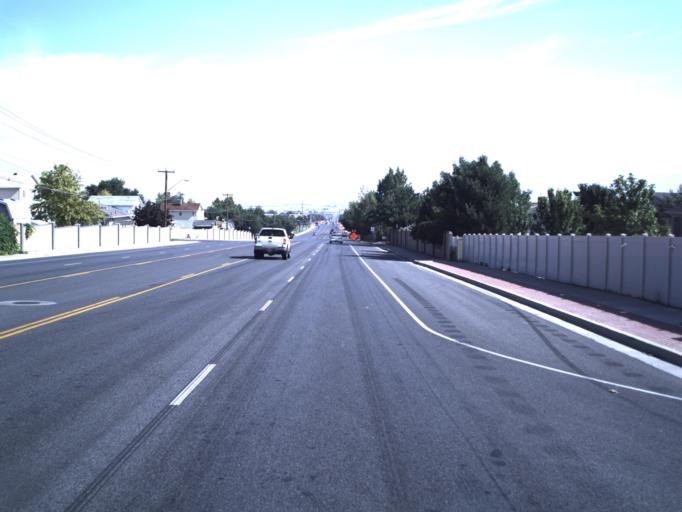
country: US
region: Utah
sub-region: Salt Lake County
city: West Valley City
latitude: 40.6732
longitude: -112.0246
